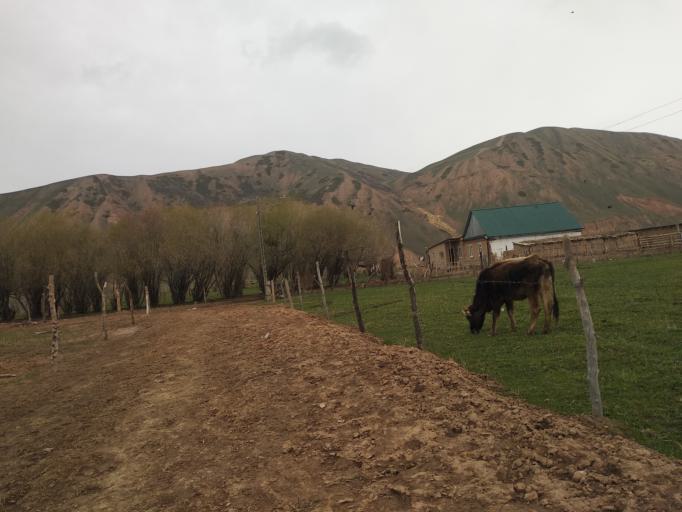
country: KG
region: Naryn
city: Naryn
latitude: 41.5211
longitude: 76.4364
